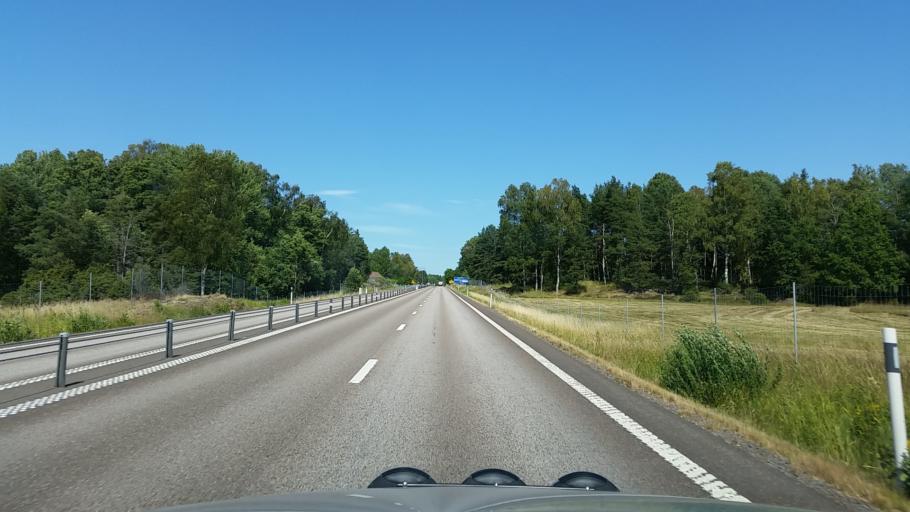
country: SE
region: Vaestra Goetaland
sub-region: Melleruds Kommun
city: Mellerud
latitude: 58.8373
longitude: 12.5403
